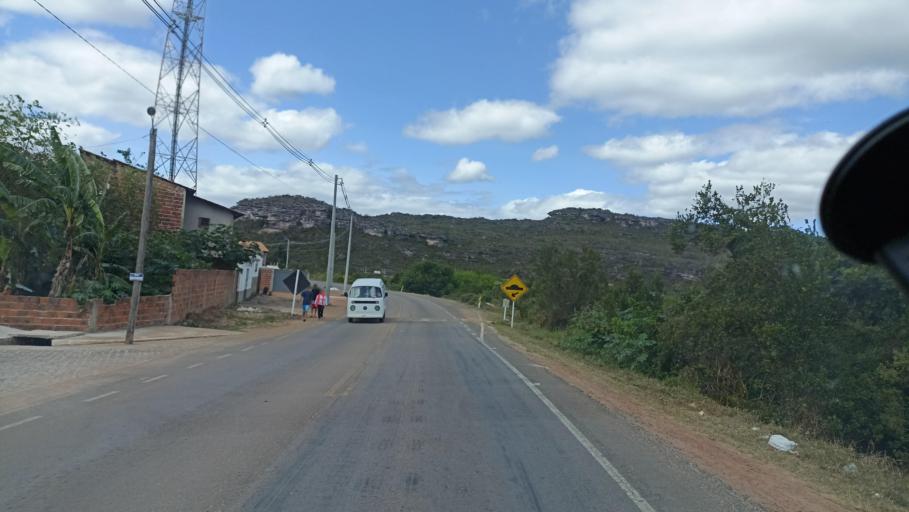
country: BR
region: Bahia
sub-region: Andarai
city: Vera Cruz
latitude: -13.0136
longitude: -41.3721
